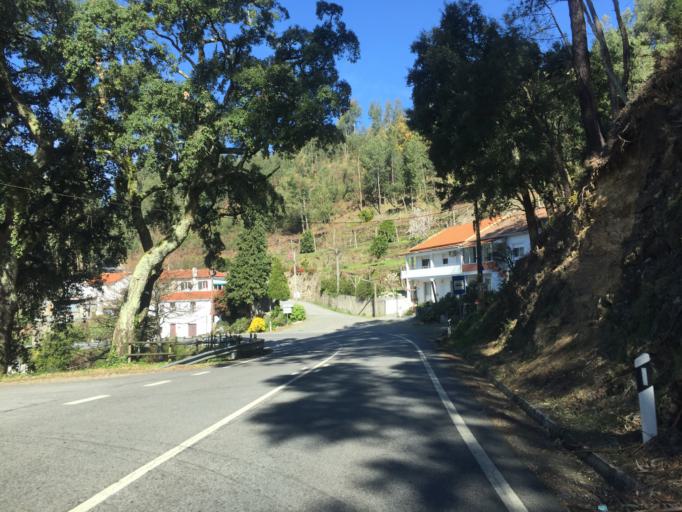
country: PT
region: Aveiro
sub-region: Vale de Cambra
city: Macieira de Cambra
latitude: 40.8977
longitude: -8.3283
